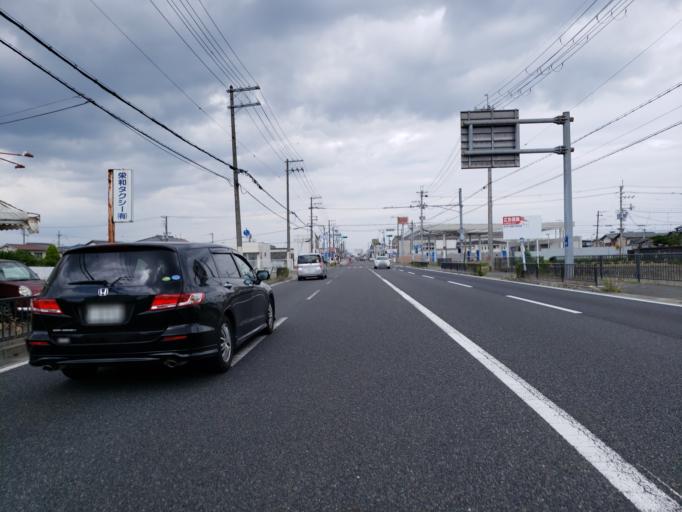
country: JP
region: Hyogo
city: Tatsunocho-tominaga
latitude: 34.7825
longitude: 134.5784
